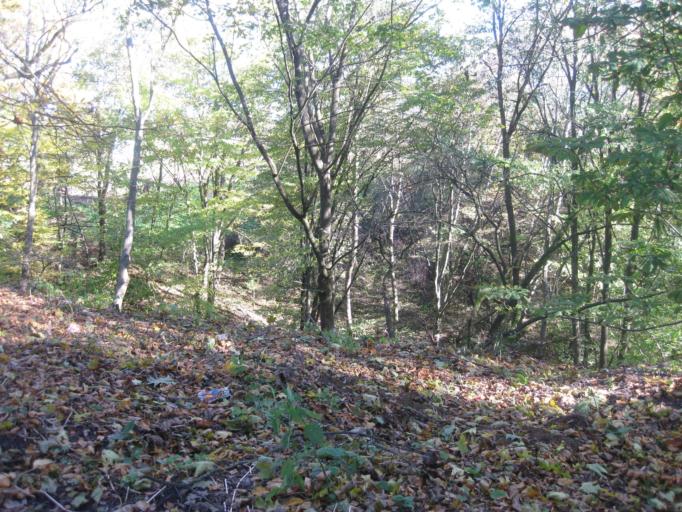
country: LT
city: Vilkija
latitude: 55.0436
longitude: 23.5756
